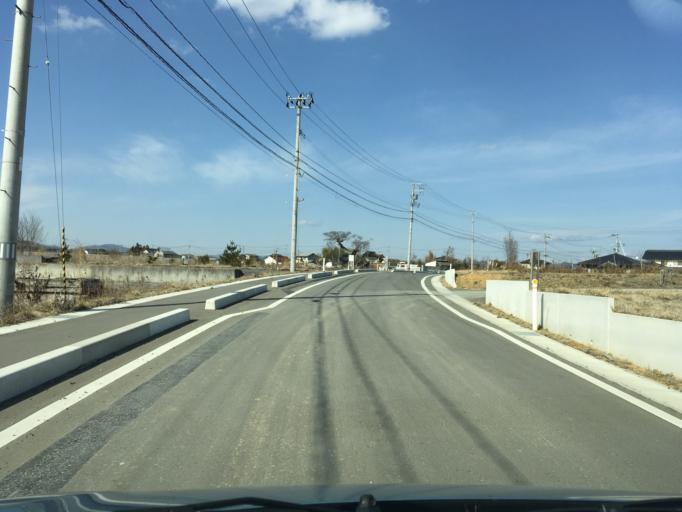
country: JP
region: Iwate
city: Ofunato
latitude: 38.8293
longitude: 141.5854
